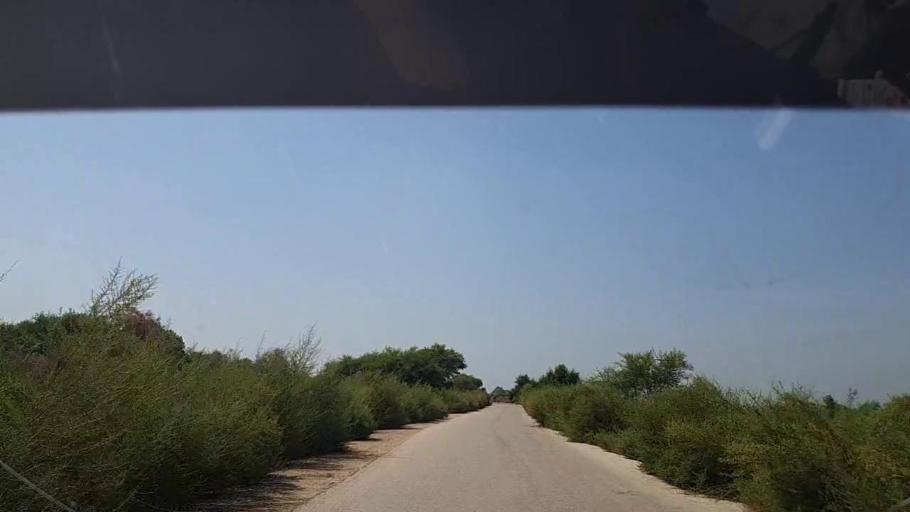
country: PK
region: Sindh
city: Ghauspur
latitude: 28.1539
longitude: 69.1593
